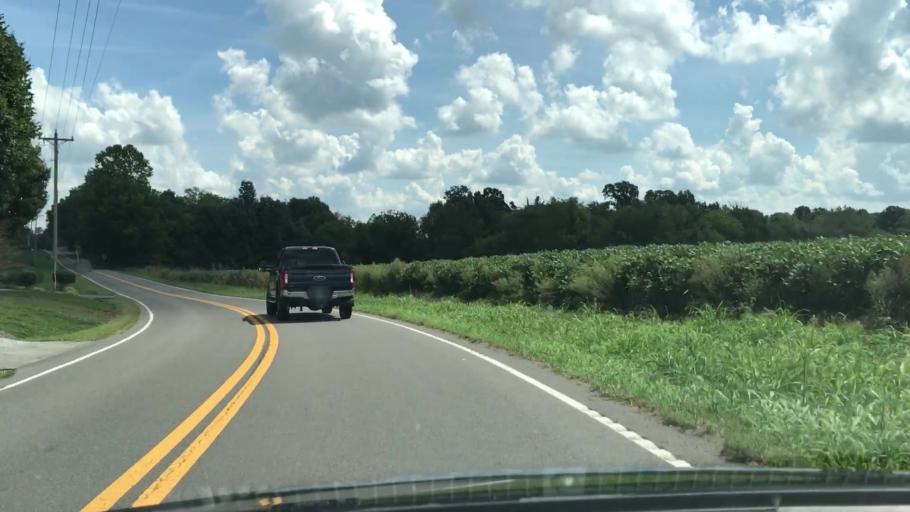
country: US
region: Tennessee
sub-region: Robertson County
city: Springfield
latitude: 36.5553
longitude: -86.8254
